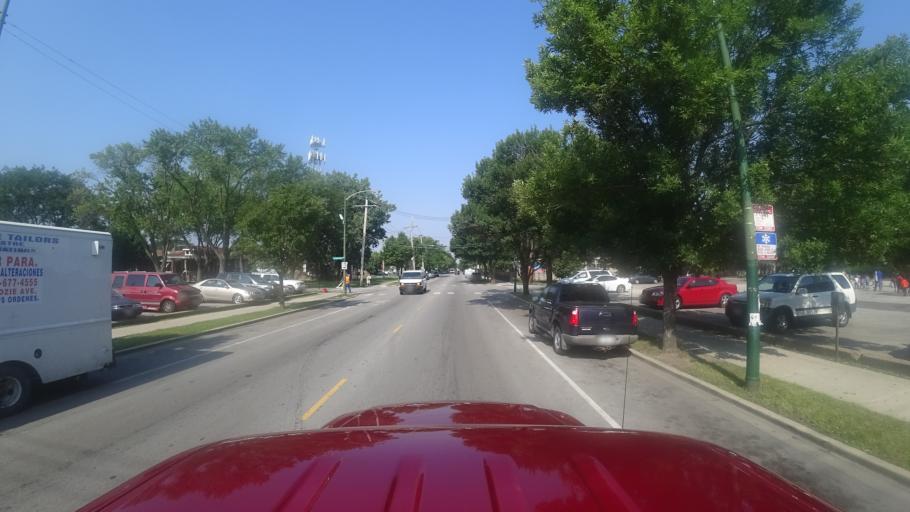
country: US
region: Illinois
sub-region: Cook County
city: Hometown
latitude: 41.7863
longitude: -87.7040
